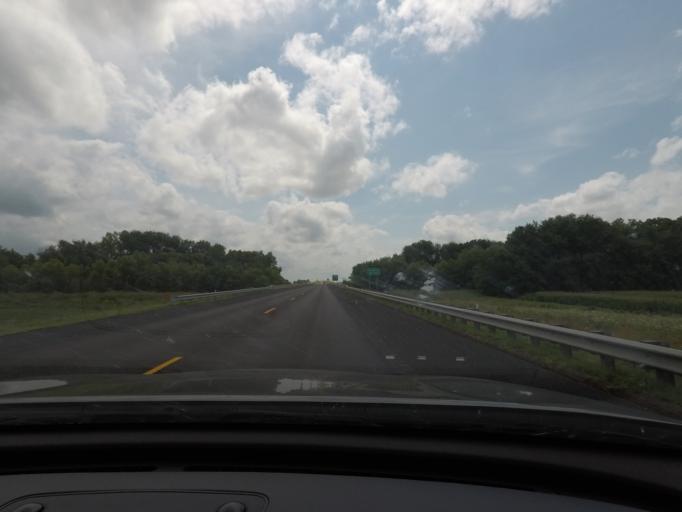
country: US
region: Missouri
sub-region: Carroll County
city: Carrollton
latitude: 39.3441
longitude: -93.4848
